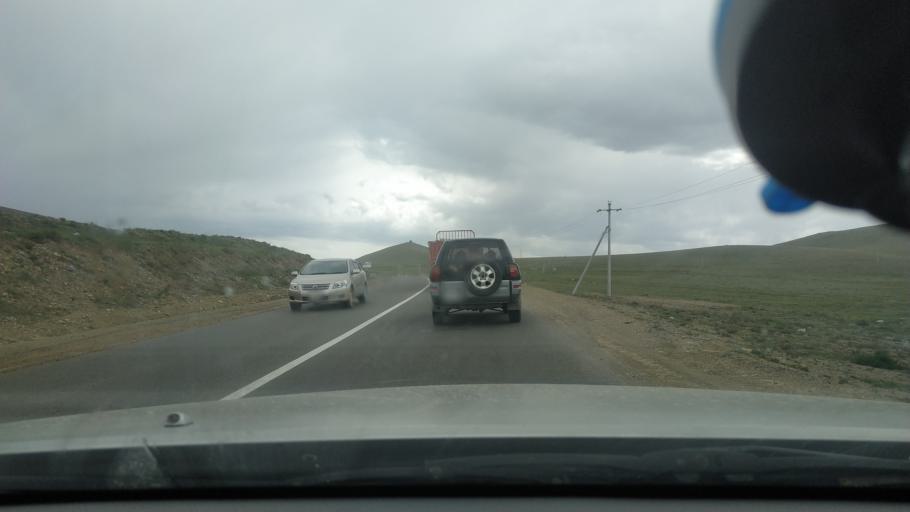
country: MN
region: Ulaanbaatar
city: Ulaanbaatar
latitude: 47.7938
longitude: 106.7451
